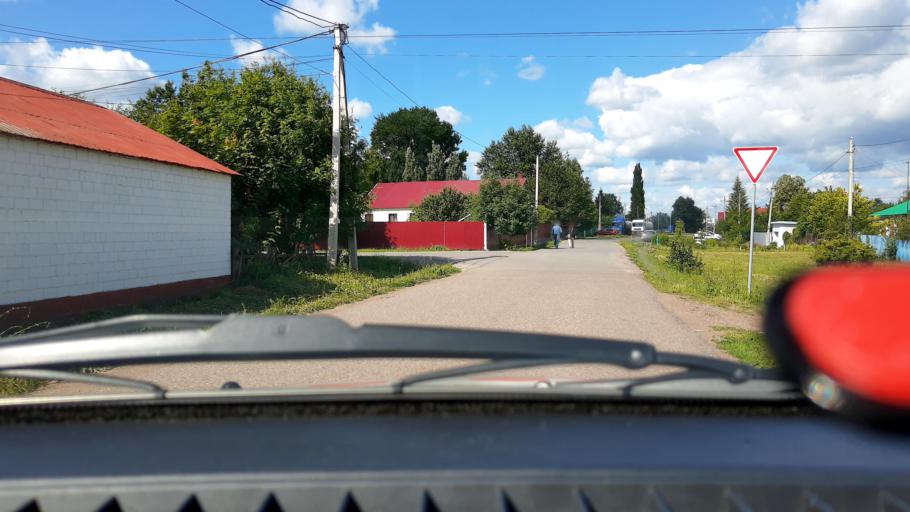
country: RU
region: Bashkortostan
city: Avdon
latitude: 54.4969
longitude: 55.8968
